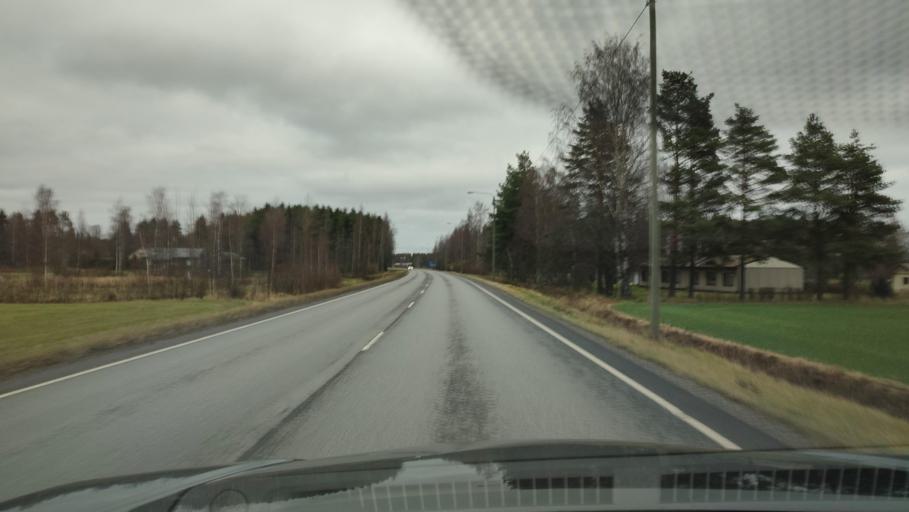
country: FI
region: Southern Ostrobothnia
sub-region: Seinaejoki
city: Kurikka
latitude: 62.6782
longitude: 22.4727
